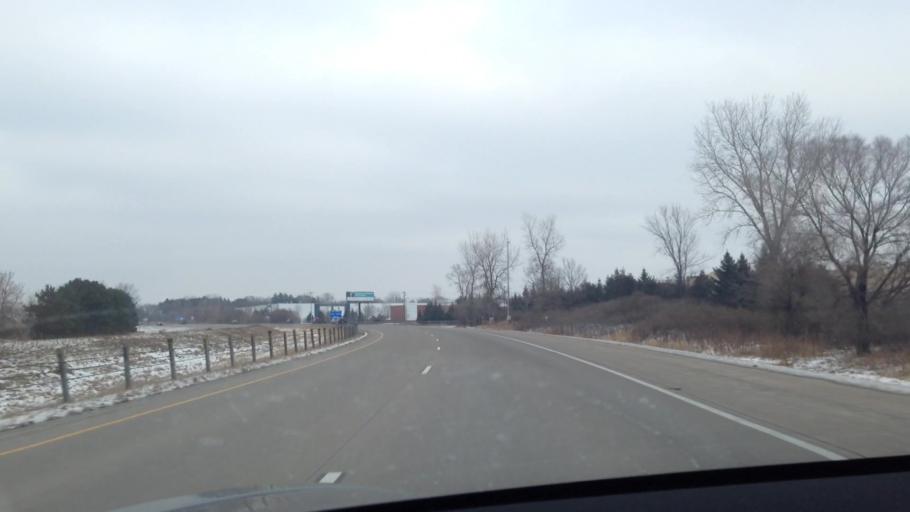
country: US
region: Minnesota
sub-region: Anoka County
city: Circle Pines
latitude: 45.1720
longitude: -93.1264
